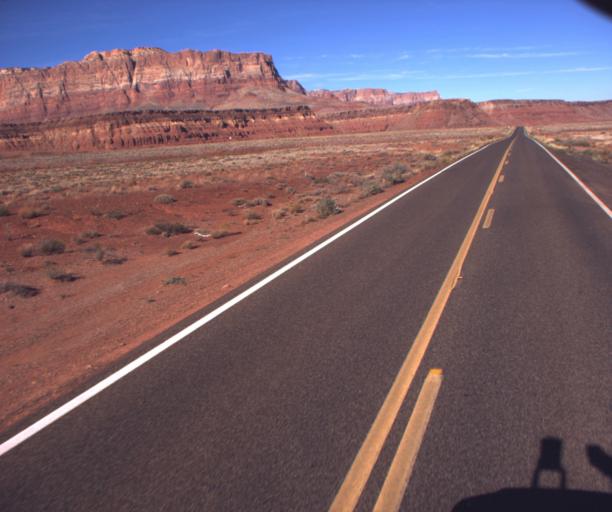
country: US
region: Arizona
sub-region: Coconino County
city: Page
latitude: 36.7277
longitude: -111.7630
